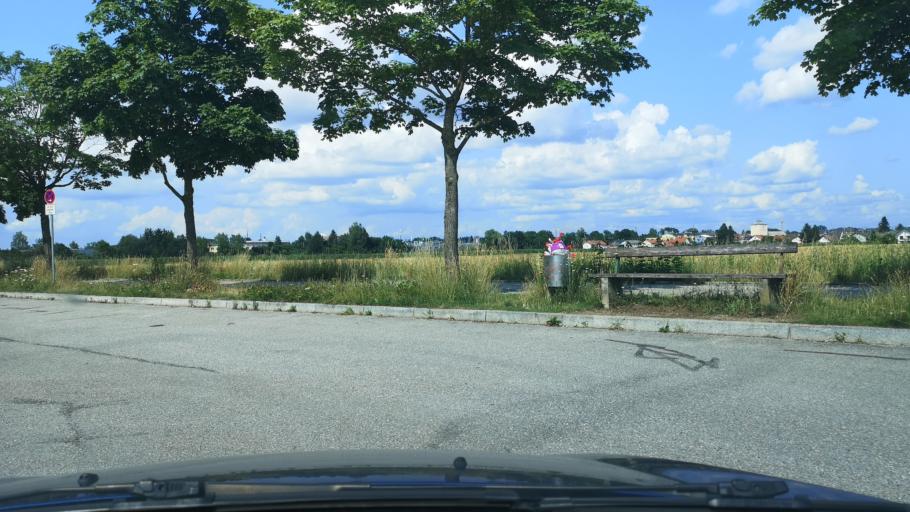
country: DE
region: Bavaria
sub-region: Upper Bavaria
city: Poing
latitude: 48.1663
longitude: 11.8030
